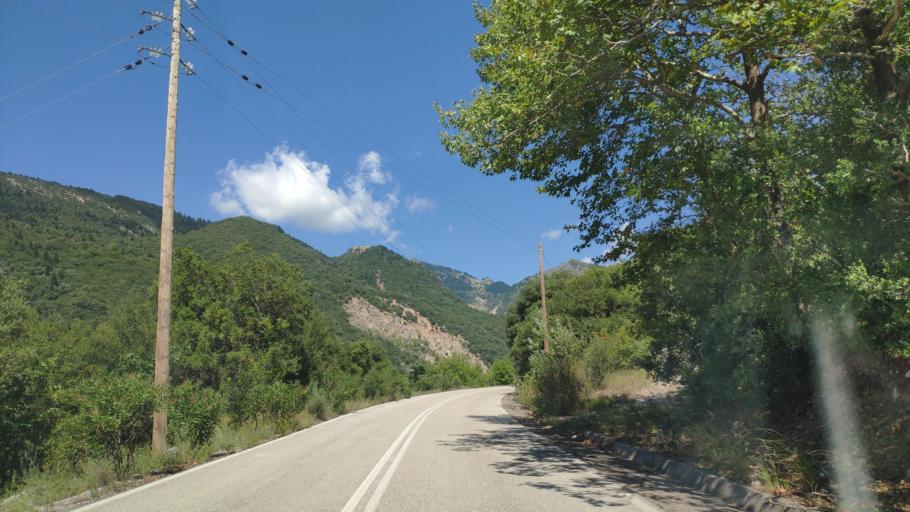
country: GR
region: Central Greece
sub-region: Nomos Evrytanias
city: Kerasochori
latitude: 39.0308
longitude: 21.6004
